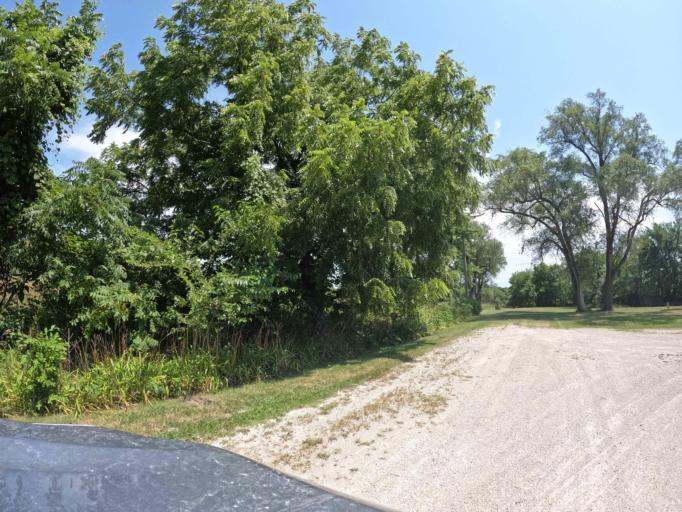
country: US
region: Iowa
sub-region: Appanoose County
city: Centerville
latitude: 40.7840
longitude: -92.9047
